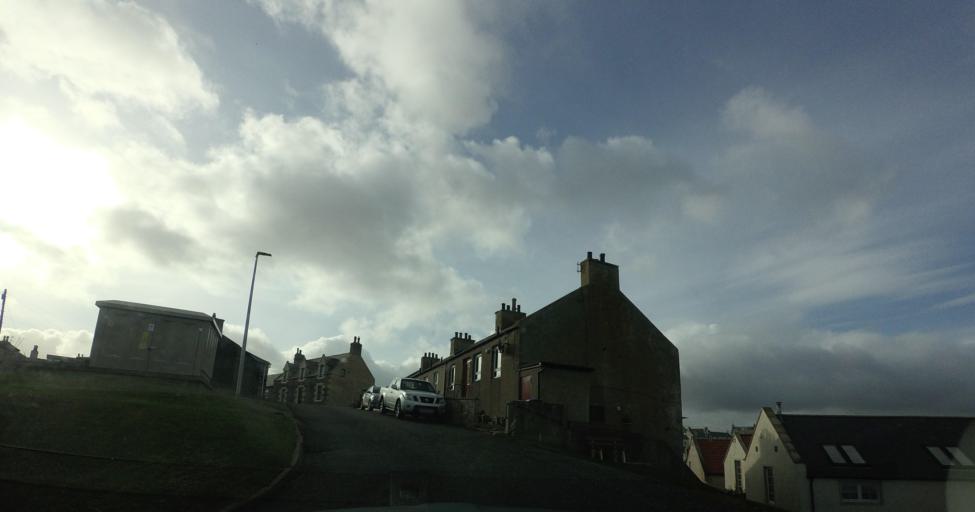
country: GB
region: Scotland
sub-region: Aberdeenshire
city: Portsoy
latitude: 57.6852
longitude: -2.6884
